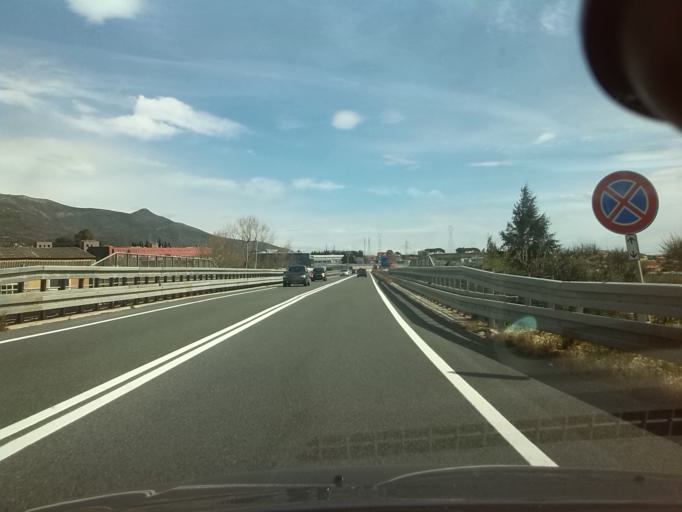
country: IT
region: Liguria
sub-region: Provincia di Savona
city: San Fedele-Lusignano
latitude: 44.0664
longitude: 8.1658
